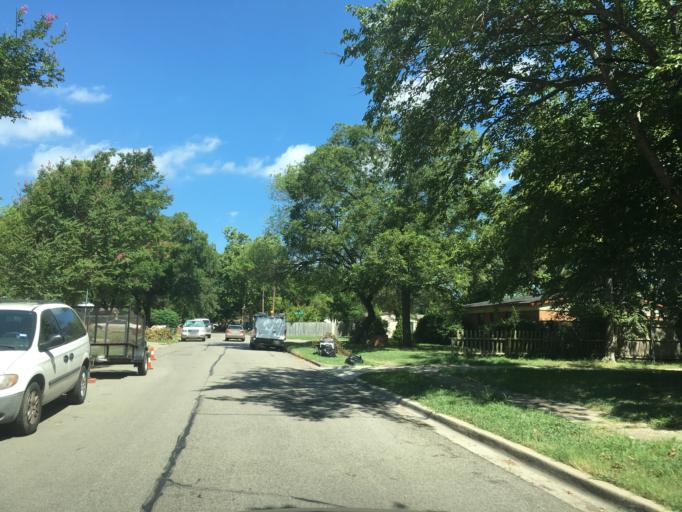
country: US
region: Texas
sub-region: Dallas County
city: Garland
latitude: 32.8346
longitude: -96.6826
